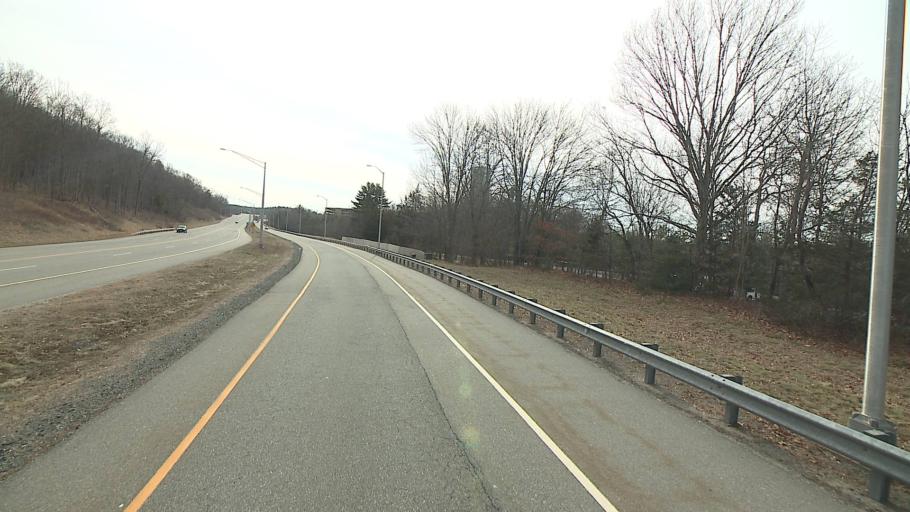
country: US
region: Connecticut
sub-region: New London County
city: Preston City
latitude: 41.4819
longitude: -71.9679
